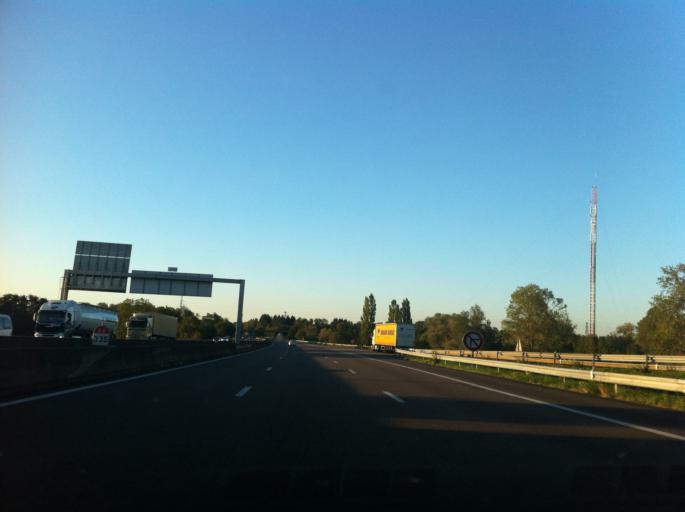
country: FR
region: Bourgogne
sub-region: Departement de Saone-et-Loire
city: Saint-Remy
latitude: 46.7521
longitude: 4.8317
